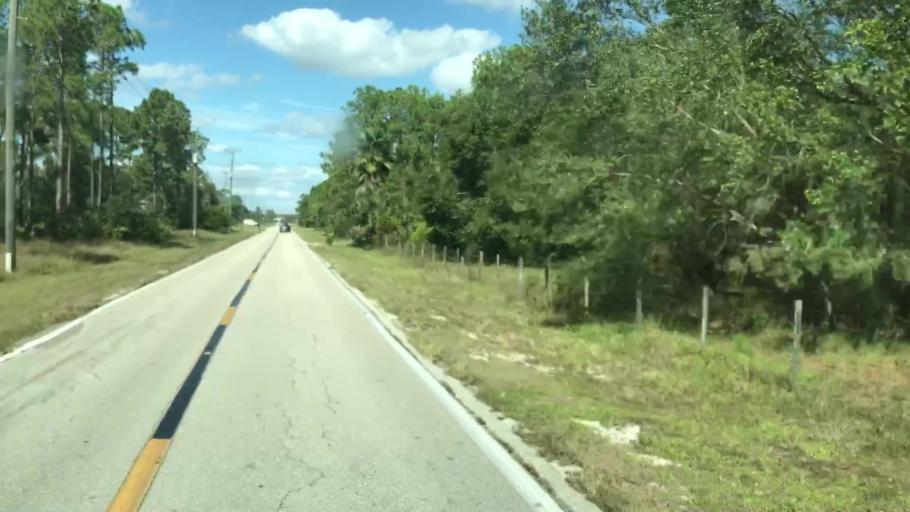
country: US
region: Florida
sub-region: Lee County
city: Lehigh Acres
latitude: 26.6635
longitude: -81.6256
